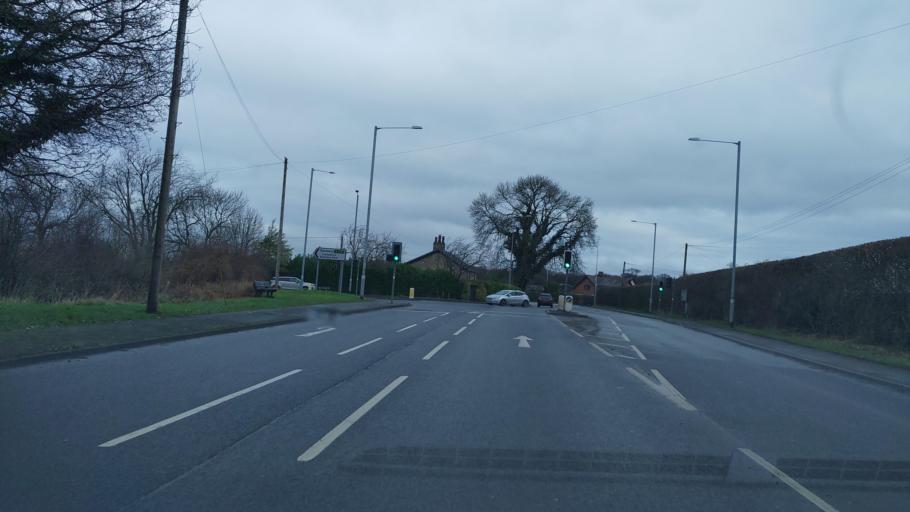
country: GB
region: England
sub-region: Lancashire
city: Clayton-le-Woods
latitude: 53.7053
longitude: -2.6717
